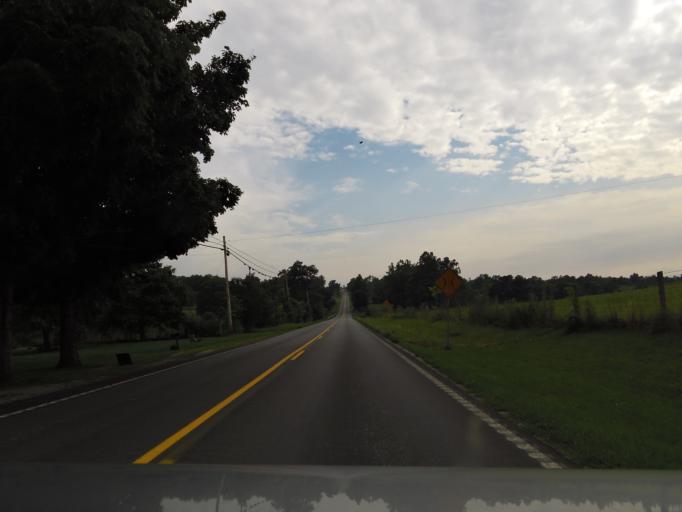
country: US
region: Kentucky
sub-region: Harrison County
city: Cynthiana
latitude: 38.4345
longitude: -84.2505
